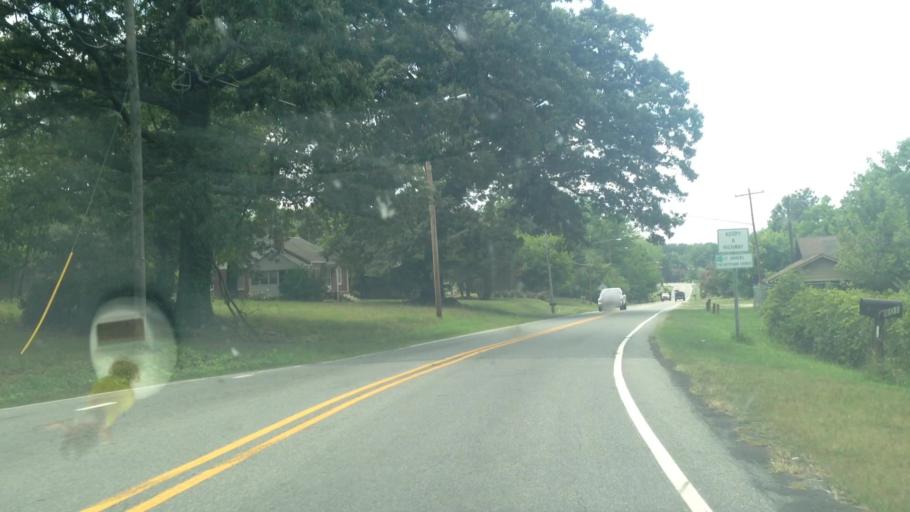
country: US
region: North Carolina
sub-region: Forsyth County
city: Rural Hall
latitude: 36.1910
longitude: -80.2455
